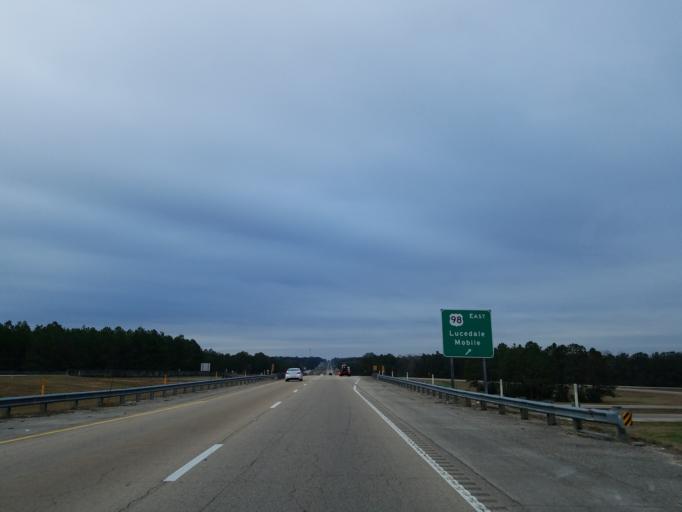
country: US
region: Mississippi
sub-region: Forrest County
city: Hattiesburg
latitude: 31.2458
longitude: -89.2765
